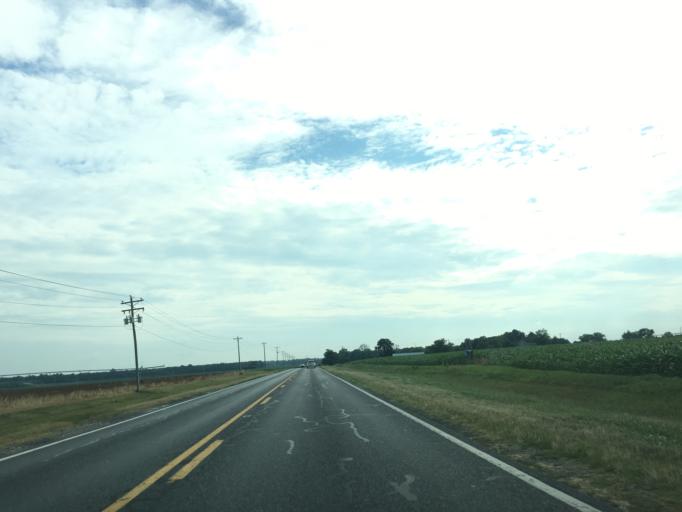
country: US
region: Delaware
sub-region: Sussex County
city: Bridgeville
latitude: 38.7582
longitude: -75.6209
